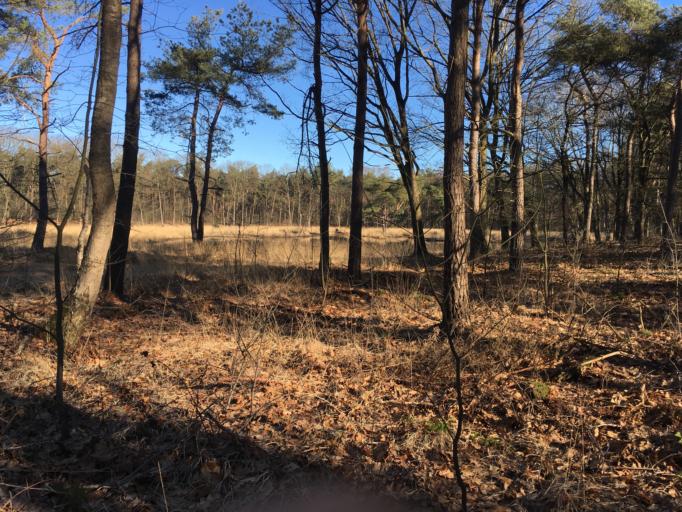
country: NL
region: North Brabant
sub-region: Gemeente Haaren
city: Haaren
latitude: 51.5503
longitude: 5.2458
